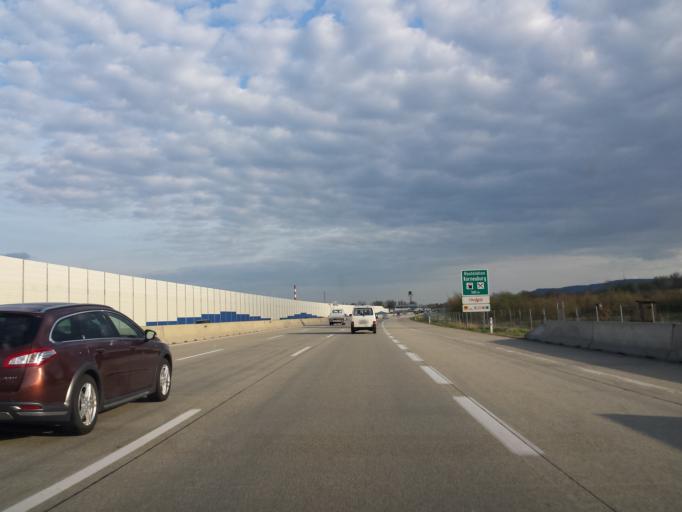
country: AT
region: Lower Austria
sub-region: Politischer Bezirk Korneuburg
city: Korneuburg
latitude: 48.3535
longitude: 16.3155
